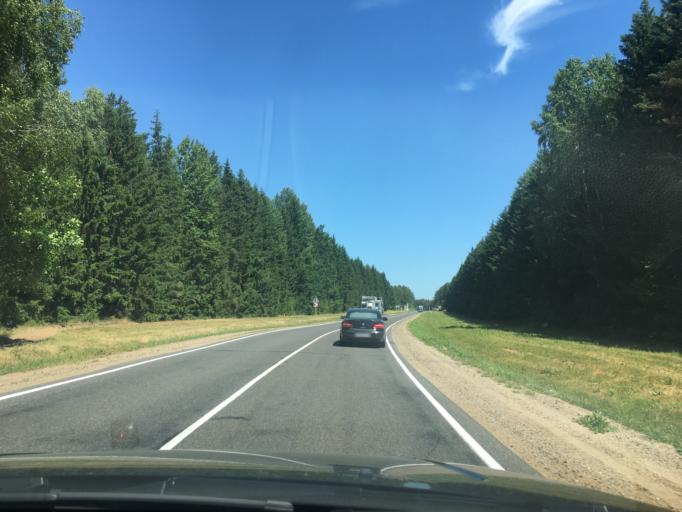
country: BY
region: Grodnenskaya
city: Hal'shany
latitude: 54.1939
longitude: 25.9438
